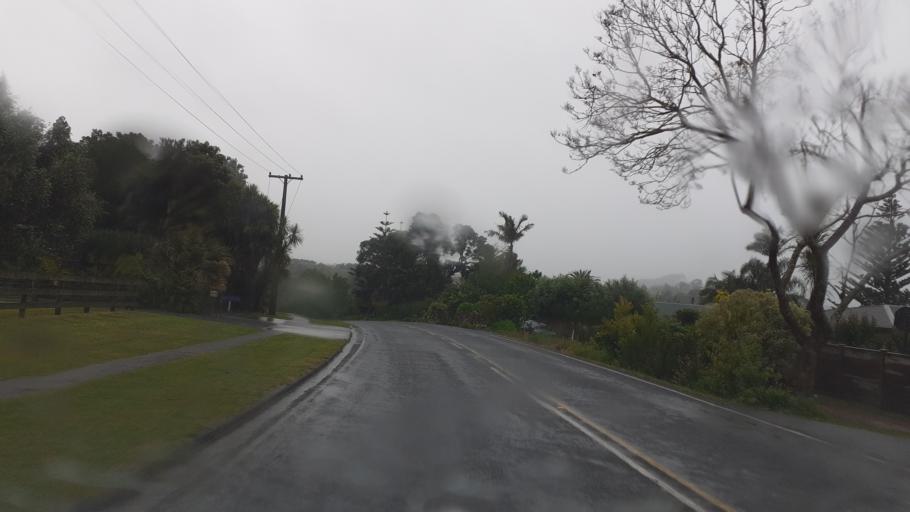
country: NZ
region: Northland
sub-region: Far North District
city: Kerikeri
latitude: -35.2064
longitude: 173.9656
